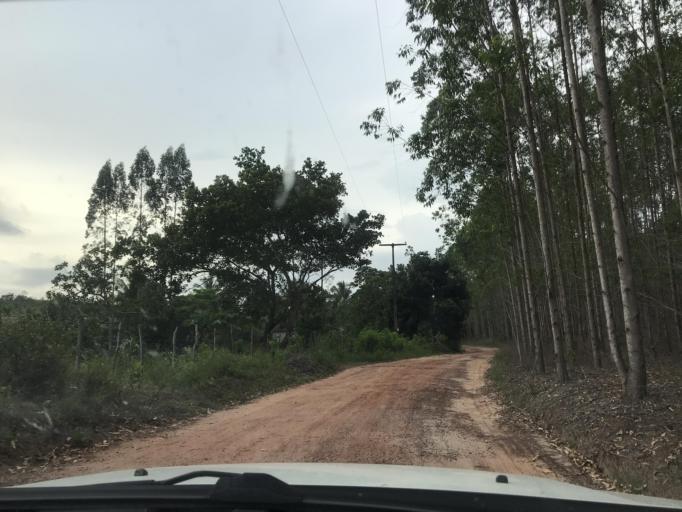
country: BR
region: Bahia
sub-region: Entre Rios
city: Entre Rios
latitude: -12.0983
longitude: -38.1901
